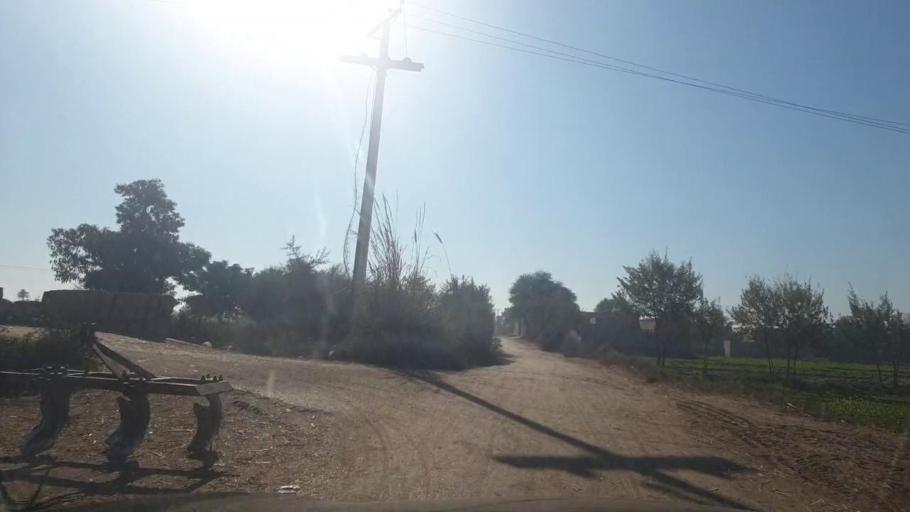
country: PK
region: Sindh
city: Ghotki
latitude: 27.9825
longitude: 69.3261
